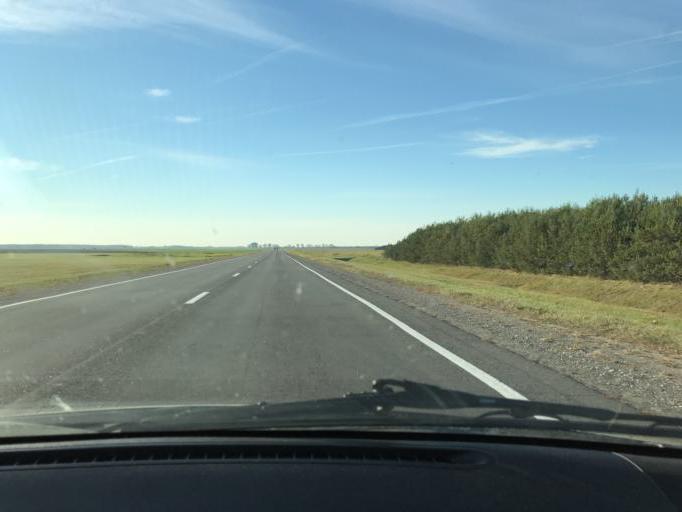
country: BY
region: Brest
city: Antopal'
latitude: 52.2221
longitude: 24.8361
